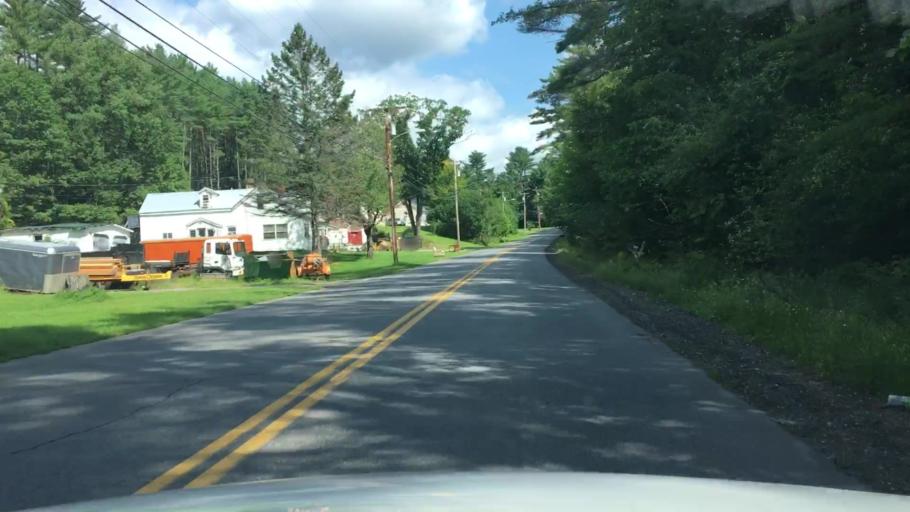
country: US
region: Maine
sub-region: Somerset County
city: Skowhegan
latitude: 44.7759
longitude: -69.7074
